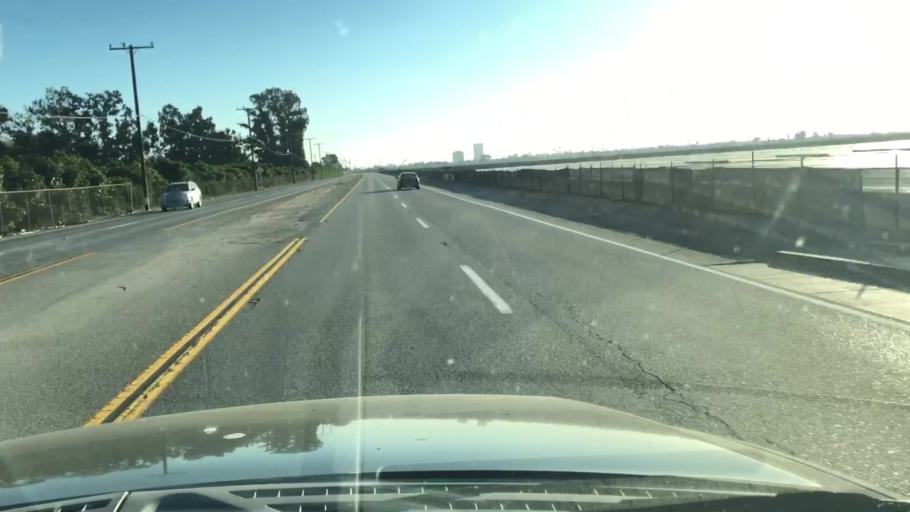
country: US
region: California
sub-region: Ventura County
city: El Rio
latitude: 34.2500
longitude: -119.1435
